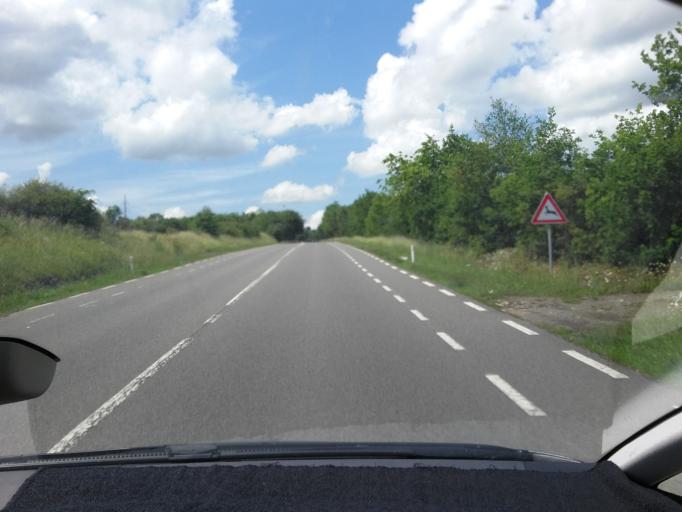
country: BE
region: Wallonia
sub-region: Province de Namur
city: Rochefort
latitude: 50.2194
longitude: 5.1846
